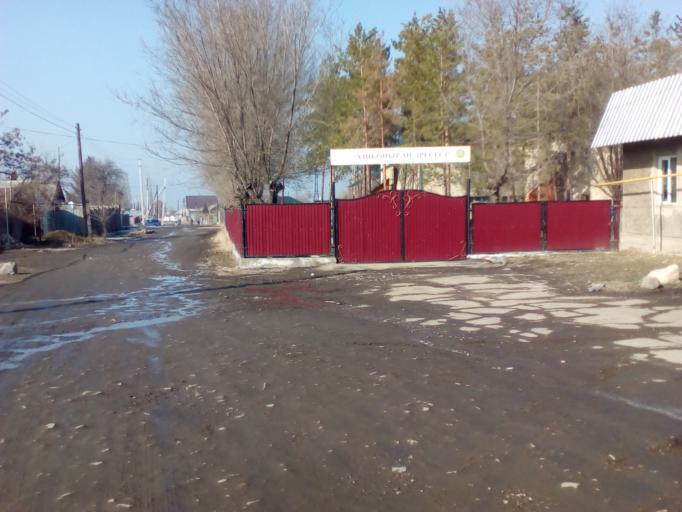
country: KZ
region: Almaty Oblysy
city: Burunday
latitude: 43.1665
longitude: 76.4123
